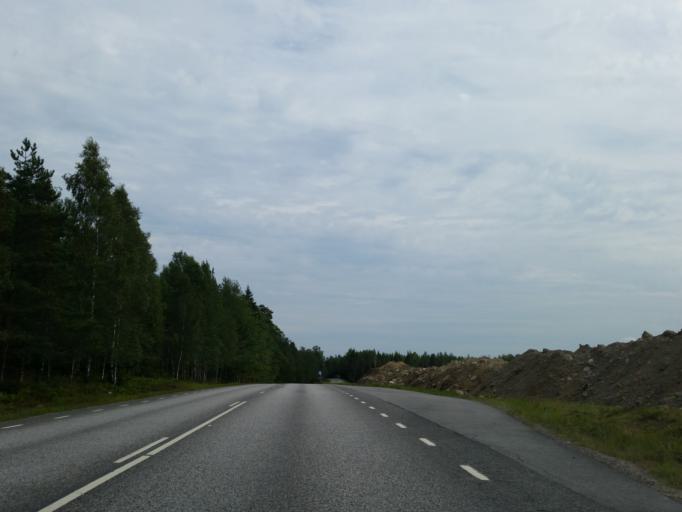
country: SE
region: Soedermanland
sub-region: Strangnas Kommun
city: Mariefred
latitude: 59.2356
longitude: 17.2004
